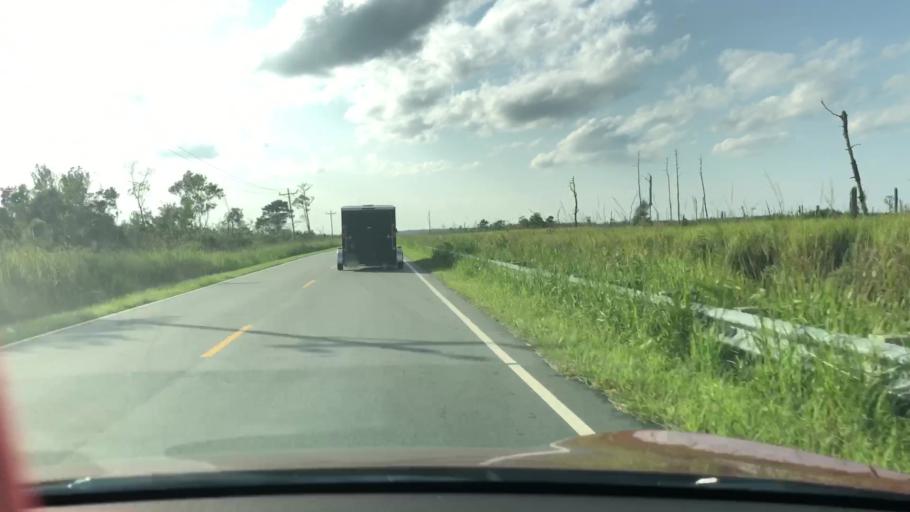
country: US
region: North Carolina
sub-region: Dare County
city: Wanchese
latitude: 35.6222
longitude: -75.8409
